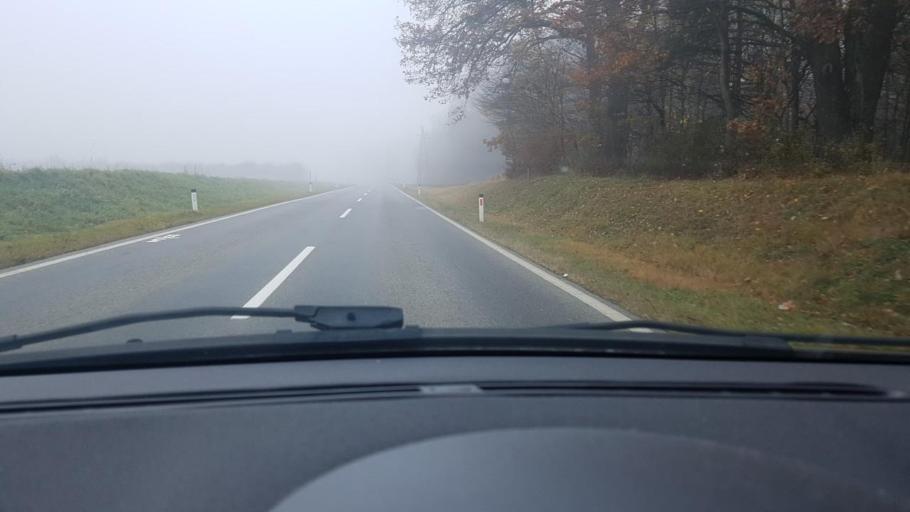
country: AT
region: Carinthia
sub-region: Politischer Bezirk Volkermarkt
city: Eberndorf
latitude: 46.5590
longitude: 14.6465
